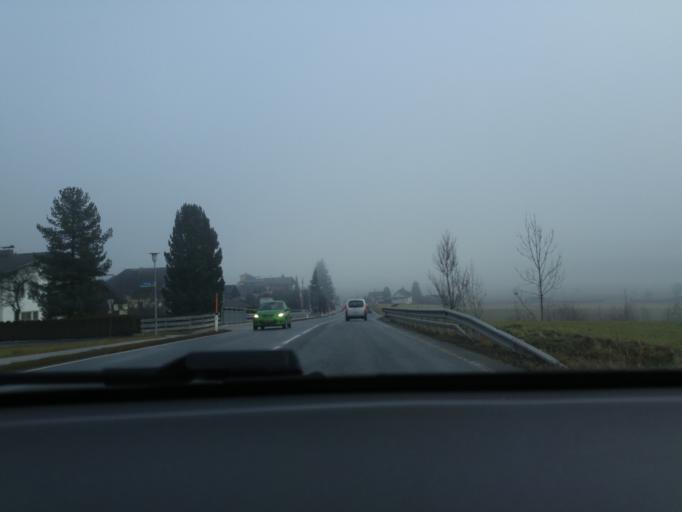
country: AT
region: Salzburg
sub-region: Politischer Bezirk Zell am See
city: Piesendorf
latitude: 47.2897
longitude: 12.6946
